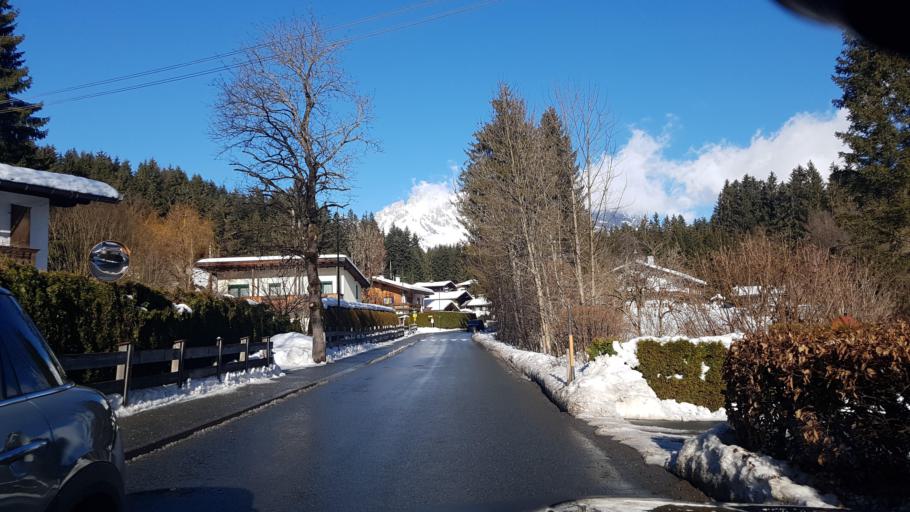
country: AT
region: Tyrol
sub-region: Politischer Bezirk Kitzbuhel
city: Oberndorf in Tirol
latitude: 47.5017
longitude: 12.3820
